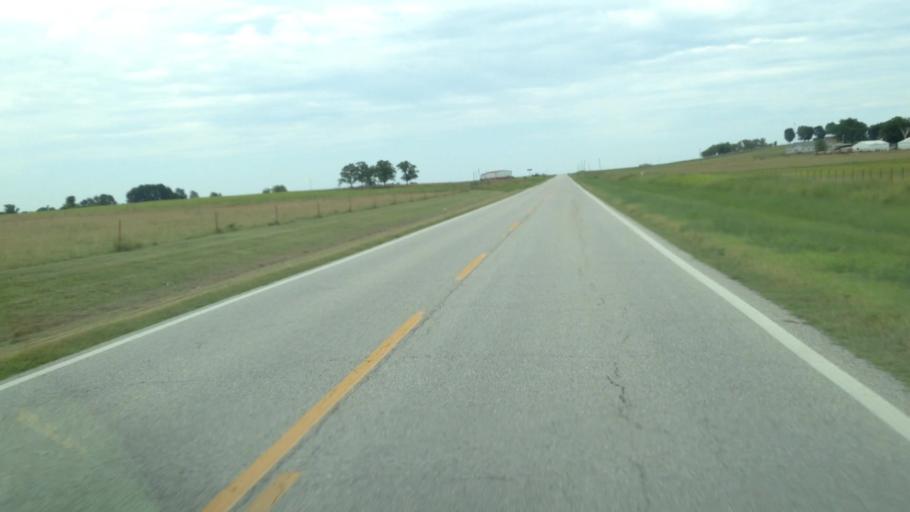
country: US
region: Oklahoma
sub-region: Craig County
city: Vinita
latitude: 36.8250
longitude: -95.1406
